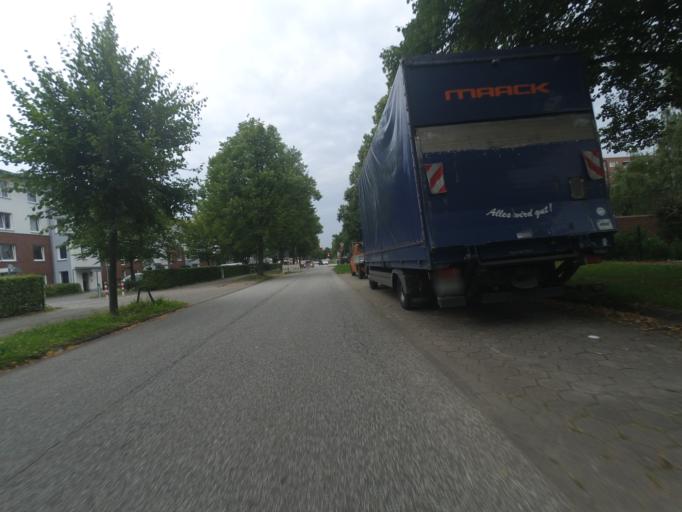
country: DE
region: Hamburg
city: Wandsbek
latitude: 53.5485
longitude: 10.0998
